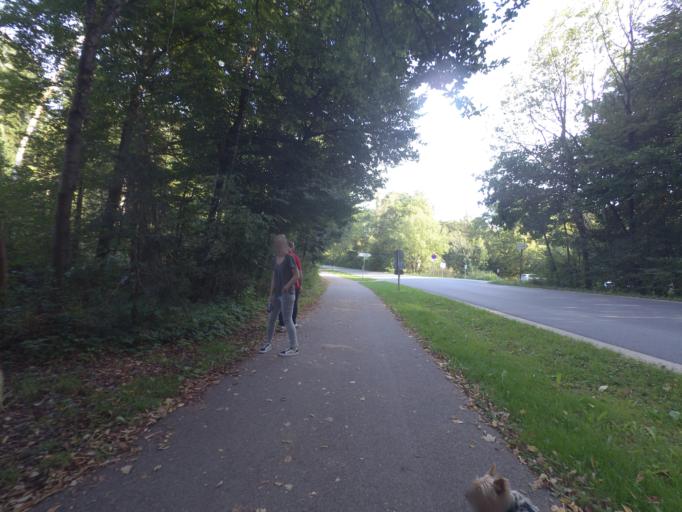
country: DE
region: Bavaria
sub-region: Upper Bavaria
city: Laufen
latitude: 47.9143
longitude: 12.9097
